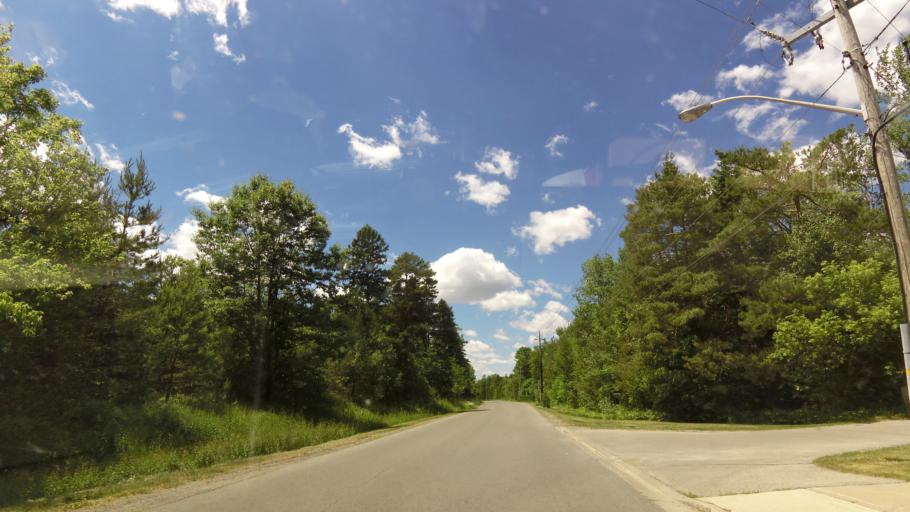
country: CA
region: Ontario
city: Oshawa
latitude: 43.9752
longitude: -78.6199
